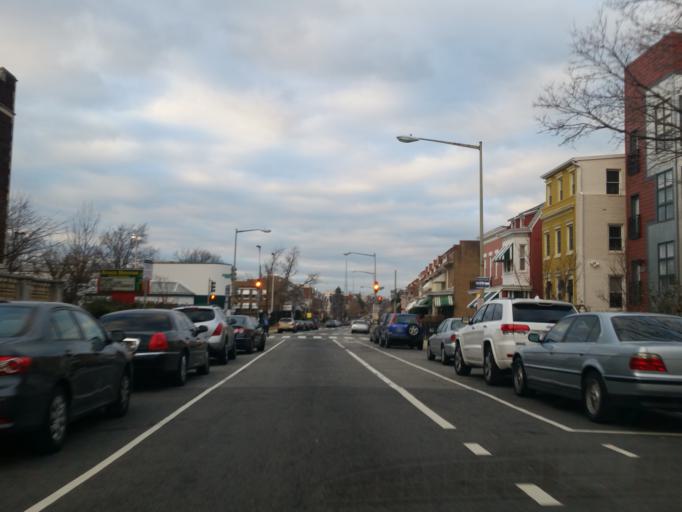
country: US
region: Maryland
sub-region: Prince George's County
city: Chillum
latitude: 38.9344
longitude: -77.0209
